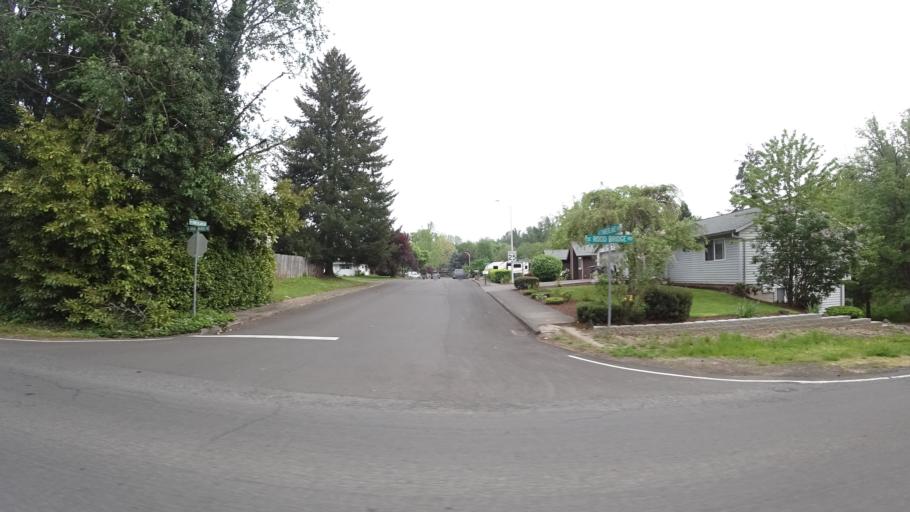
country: US
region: Oregon
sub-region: Washington County
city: Hillsboro
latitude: 45.4971
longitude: -122.9535
